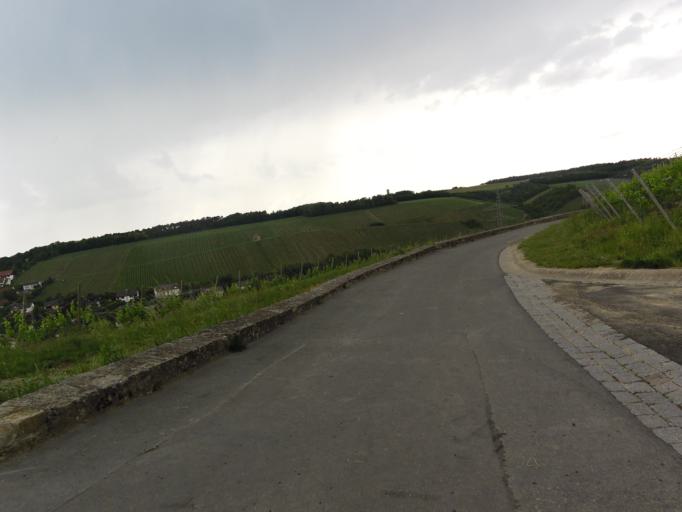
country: DE
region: Bavaria
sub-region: Regierungsbezirk Unterfranken
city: Hochberg
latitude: 49.8039
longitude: 9.9025
